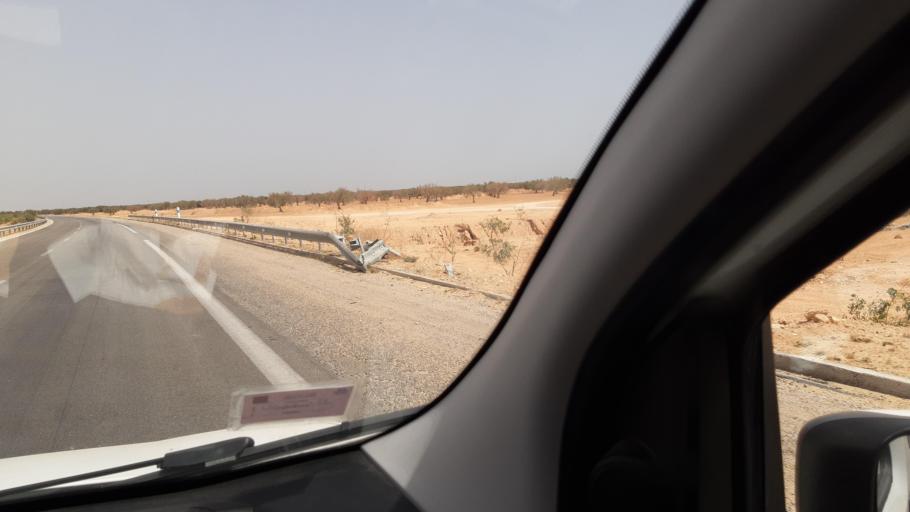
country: TN
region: Safaqis
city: Bi'r `Ali Bin Khalifah
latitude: 34.5667
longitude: 10.3706
